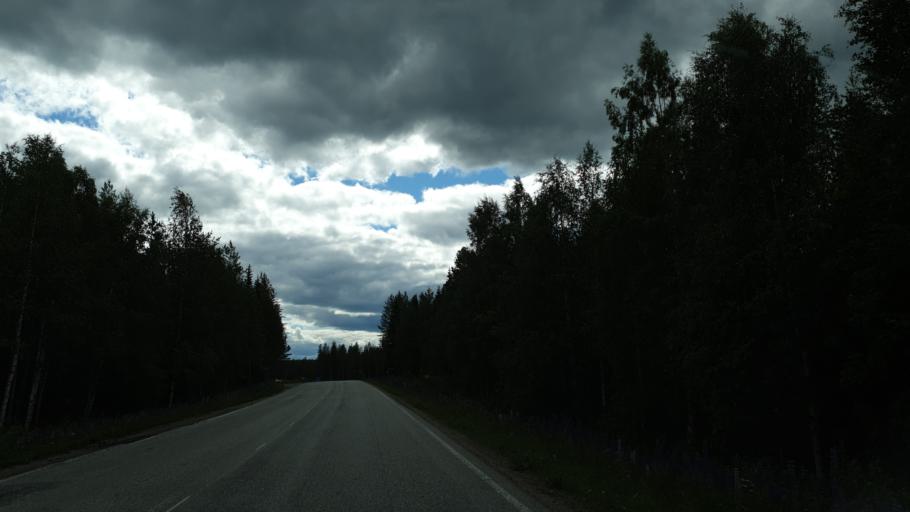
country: FI
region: Kainuu
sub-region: Kehys-Kainuu
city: Kuhmo
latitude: 63.9793
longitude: 29.6413
